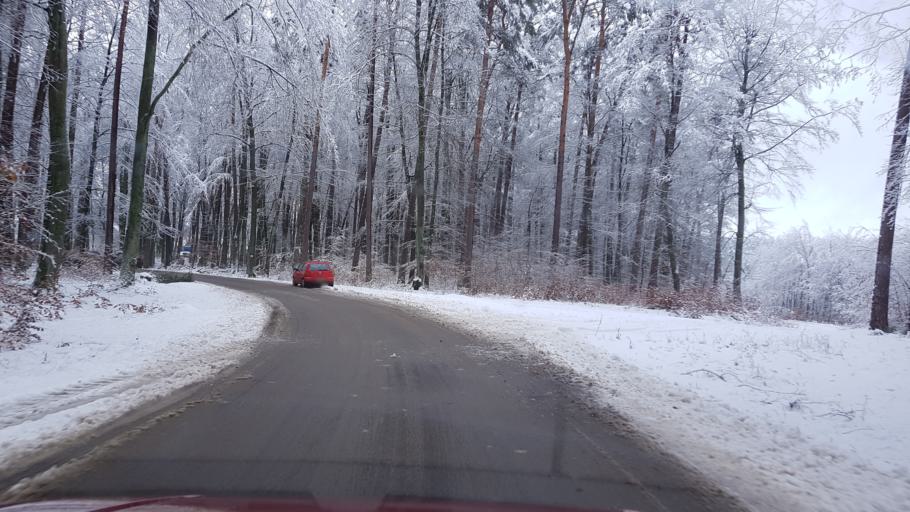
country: PL
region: West Pomeranian Voivodeship
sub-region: Powiat drawski
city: Zlocieniec
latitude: 53.5039
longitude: 15.9909
